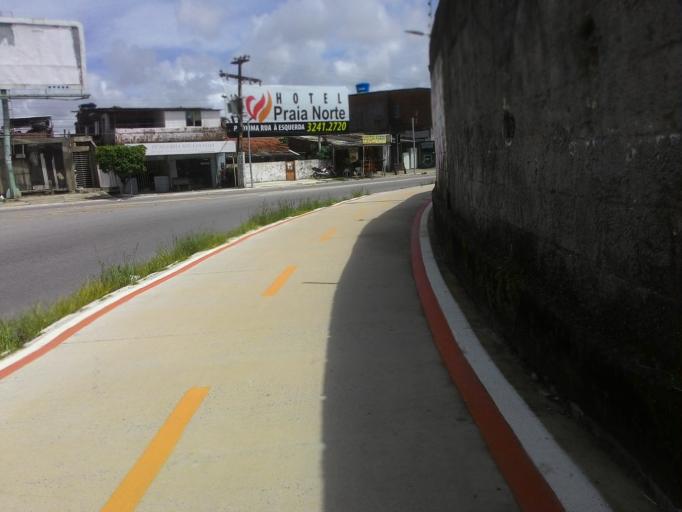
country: BR
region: Pernambuco
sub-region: Olinda
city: Olinda
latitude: -8.0298
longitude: -34.8671
